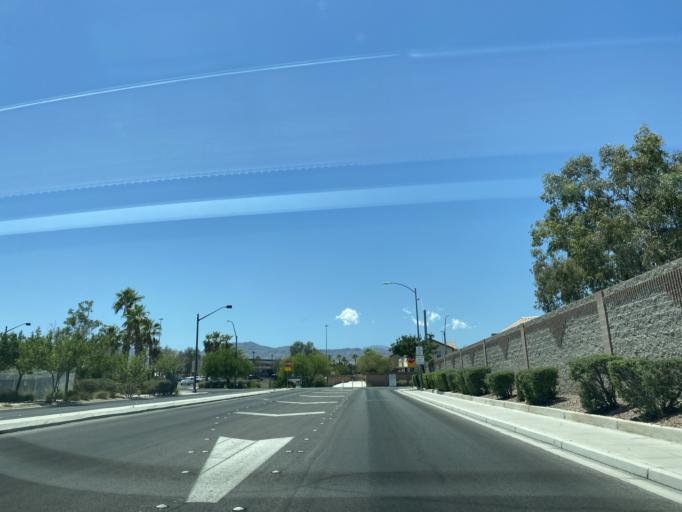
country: US
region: Nevada
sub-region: Clark County
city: Las Vegas
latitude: 36.2843
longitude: -115.2686
